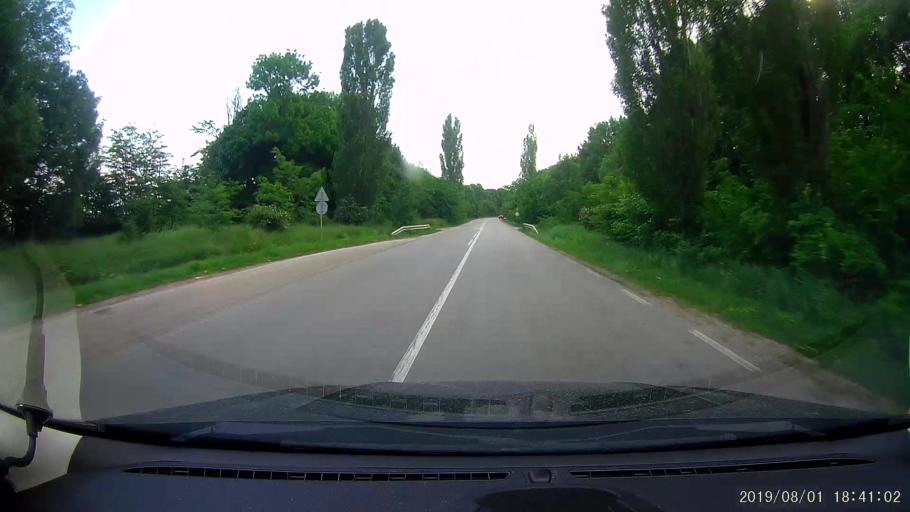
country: BG
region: Shumen
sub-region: Obshtina Khitrino
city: Gara Khitrino
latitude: 43.3534
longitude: 26.9229
